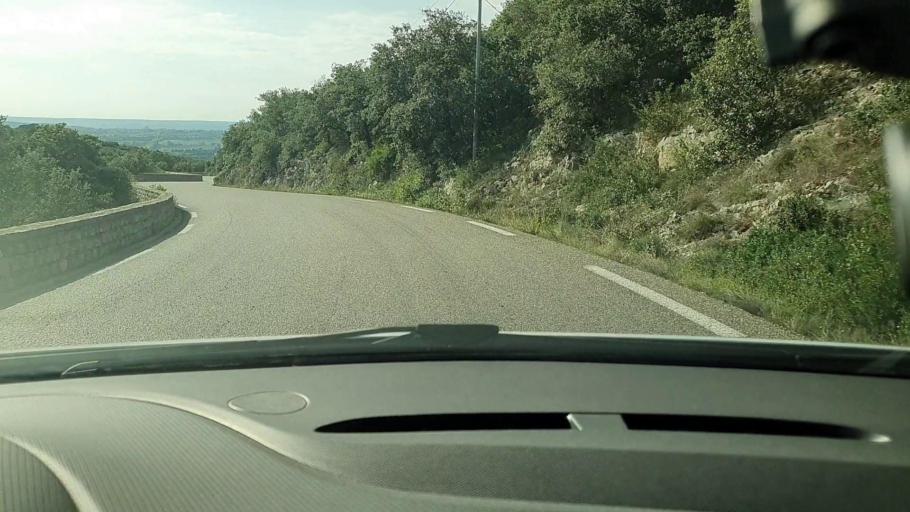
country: FR
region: Languedoc-Roussillon
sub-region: Departement du Gard
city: Montaren-et-Saint-Mediers
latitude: 44.0651
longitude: 4.3962
